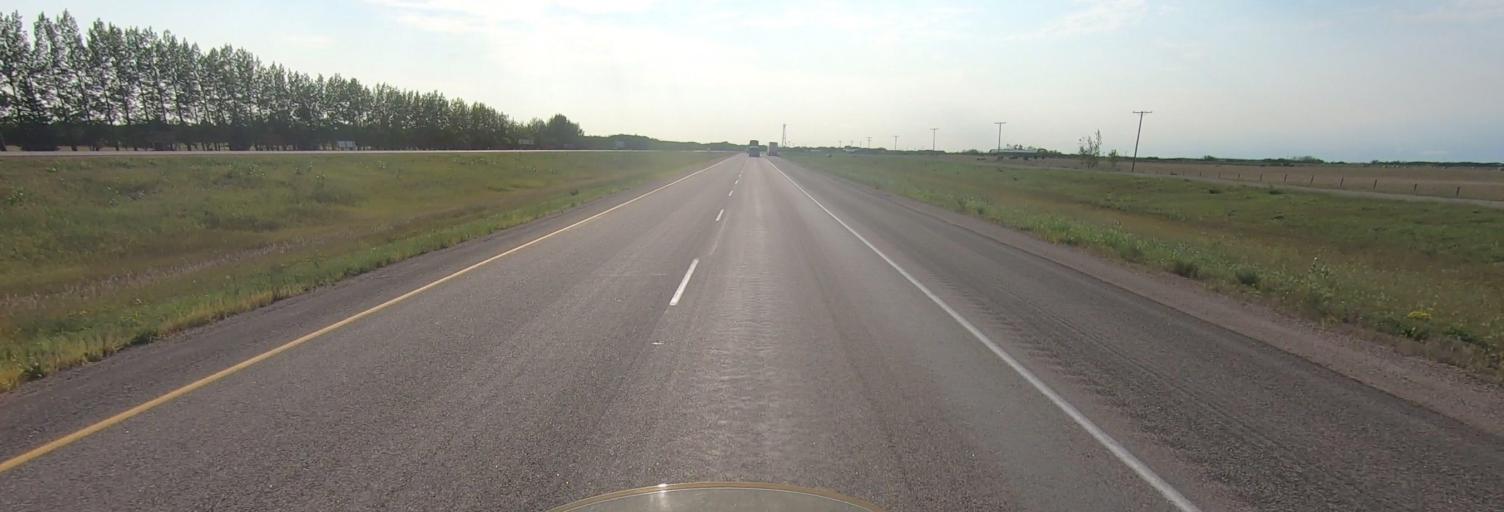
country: CA
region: Saskatchewan
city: Esterhazy
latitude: 50.3378
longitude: -102.2756
